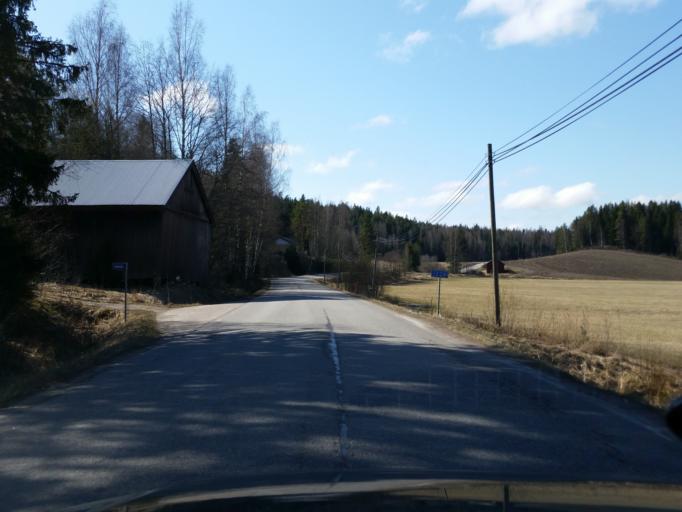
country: FI
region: Uusimaa
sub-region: Helsinki
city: Vihti
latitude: 60.4333
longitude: 24.2425
